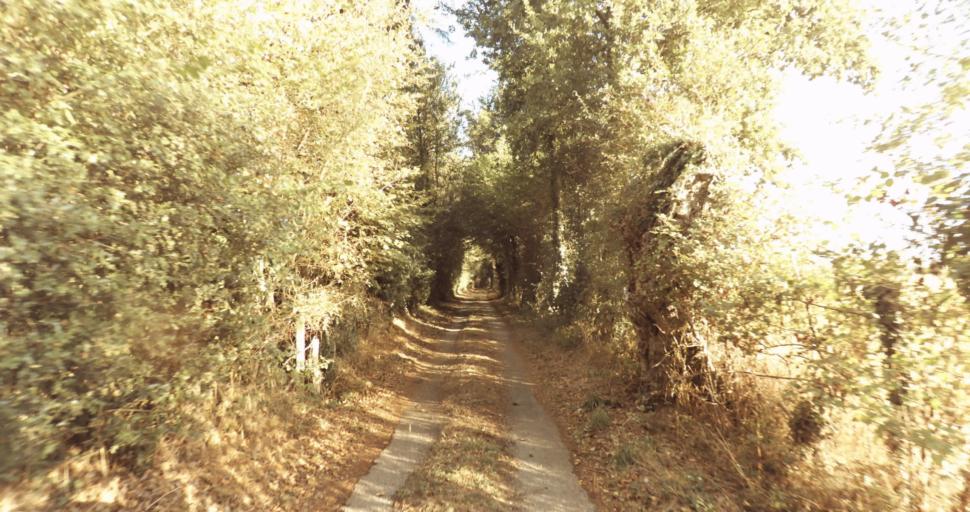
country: FR
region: Lower Normandy
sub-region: Departement de l'Orne
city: Vimoutiers
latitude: 48.9341
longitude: 0.2295
